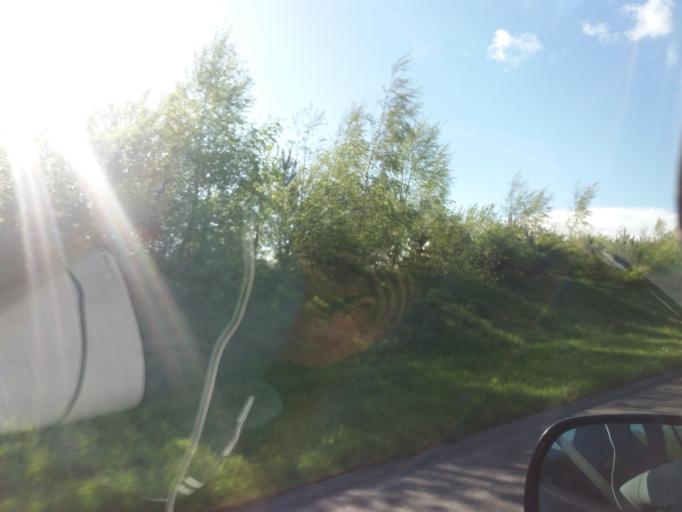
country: IE
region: Munster
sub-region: Waterford
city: Waterford
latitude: 52.3177
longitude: -7.1428
